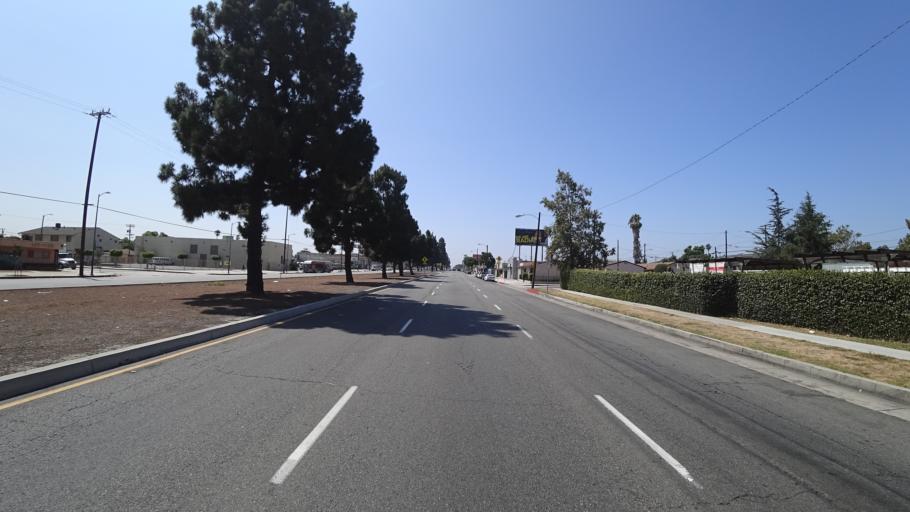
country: US
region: California
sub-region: Los Angeles County
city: Westmont
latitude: 33.9370
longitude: -118.2919
